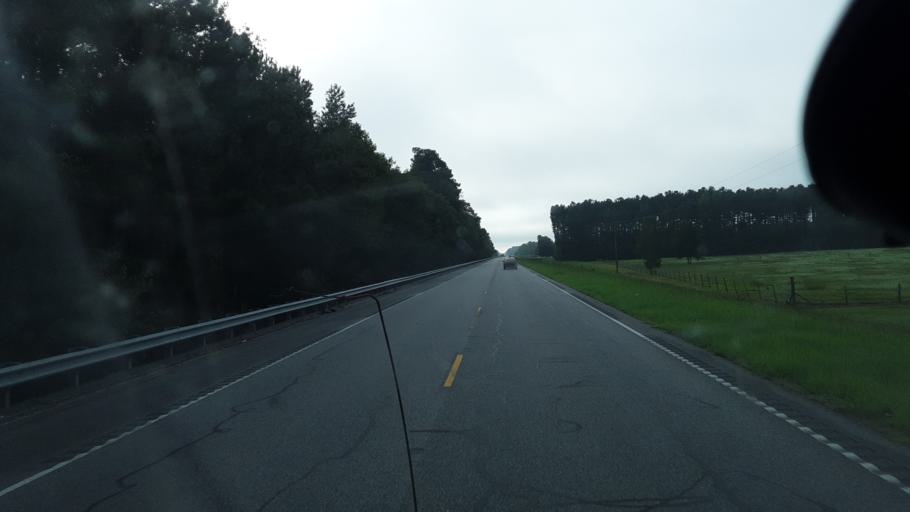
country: US
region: South Carolina
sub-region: Florence County
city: Johnsonville
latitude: 33.8542
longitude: -79.3049
